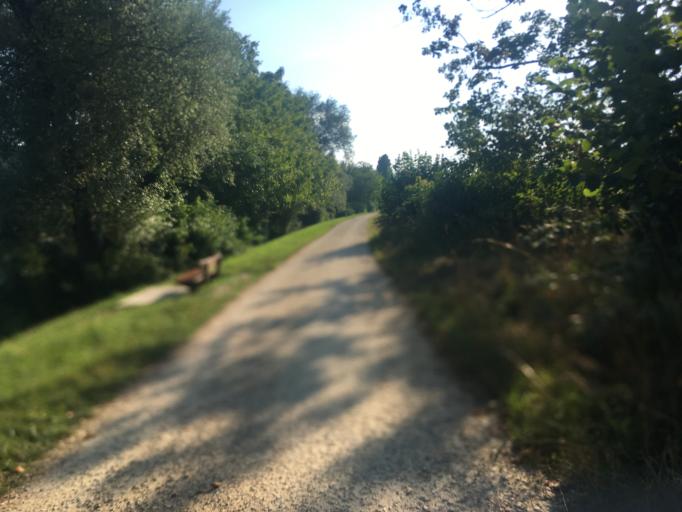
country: CH
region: Bern
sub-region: Biel/Bienne District
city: Brugg
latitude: 47.1180
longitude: 7.2727
